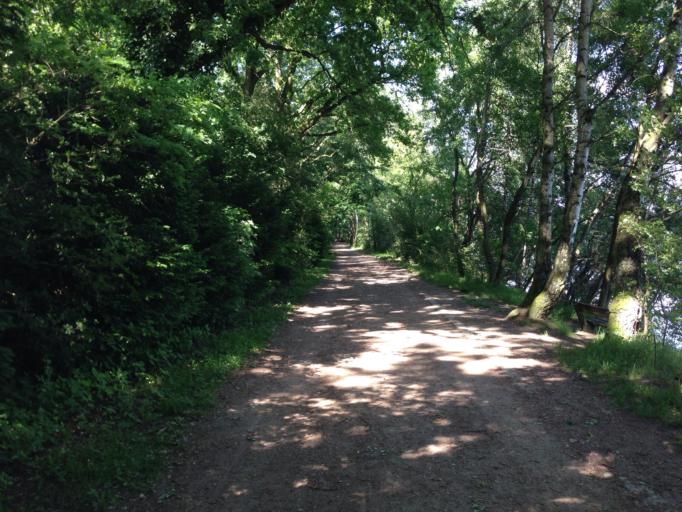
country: DE
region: Schleswig-Holstein
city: Barsbuettel
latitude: 53.5585
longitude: 10.1359
